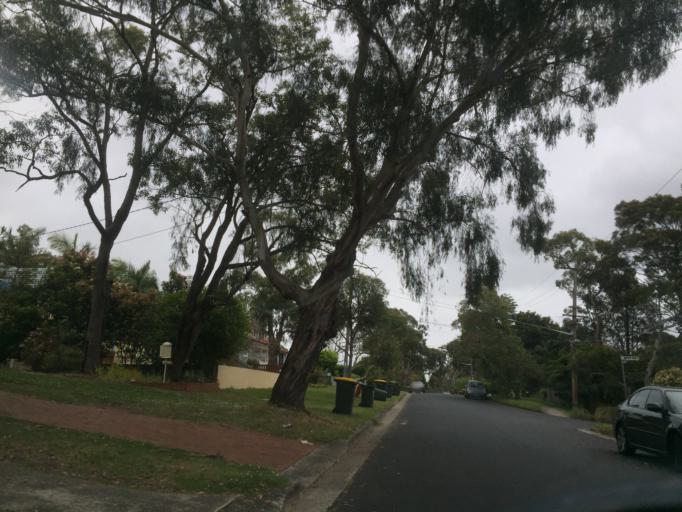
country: AU
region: New South Wales
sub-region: Willoughby
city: Lane Cove North
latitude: -33.8032
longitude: 151.1599
